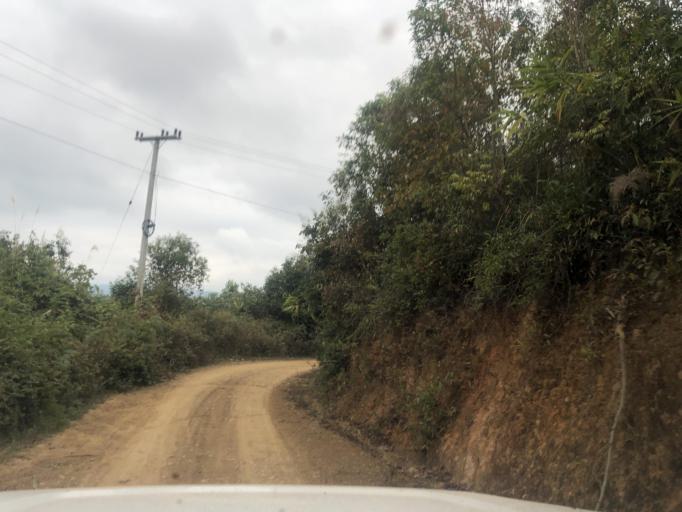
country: LA
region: Phongsali
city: Khoa
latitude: 21.2597
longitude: 102.5897
